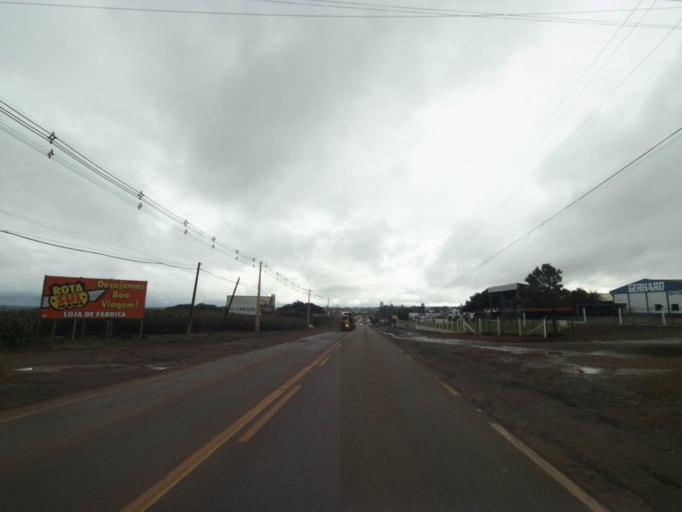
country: BR
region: Parana
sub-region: Marechal Candido Rondon
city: Marechal Candido Rondon
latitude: -24.5683
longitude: -54.0279
